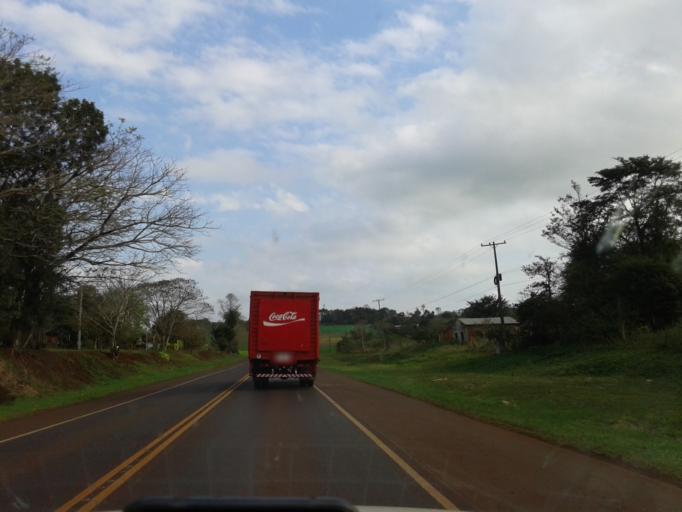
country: PY
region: Itapua
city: Edelira
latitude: -26.7163
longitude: -55.3306
